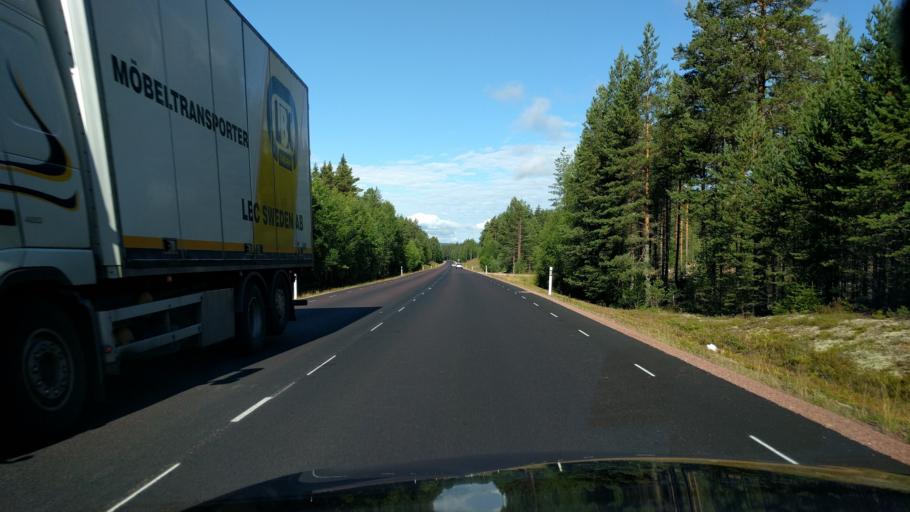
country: SE
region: Dalarna
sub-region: Alvdalens Kommun
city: AElvdalen
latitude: 61.1188
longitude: 14.2490
